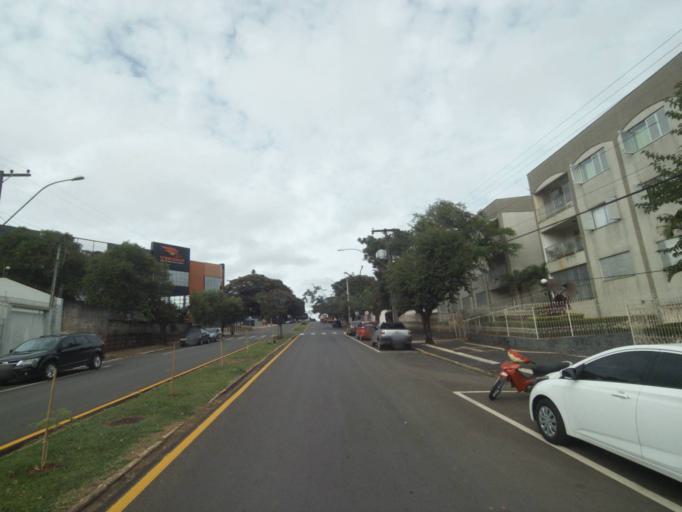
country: BR
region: Parana
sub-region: Telemaco Borba
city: Telemaco Borba
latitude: -24.3277
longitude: -50.6186
